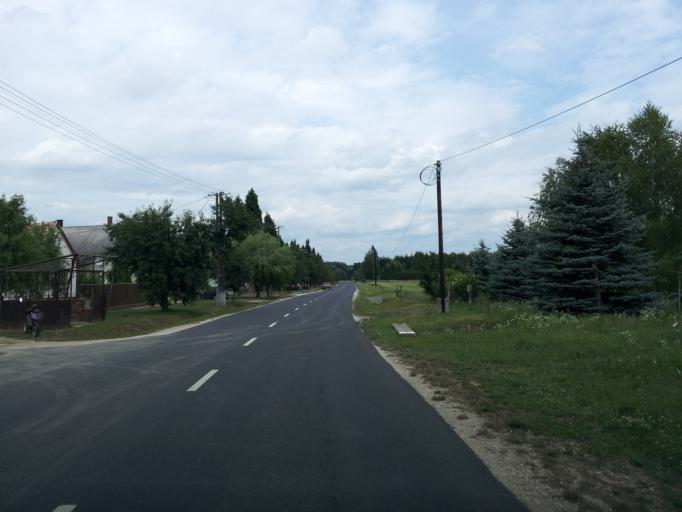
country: HU
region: Zala
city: Zalaszentgrot
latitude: 47.0352
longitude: 16.9809
